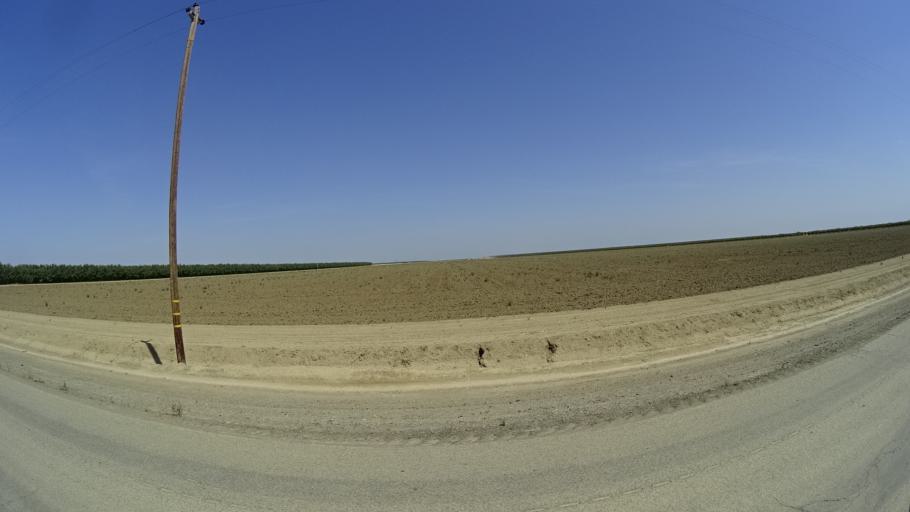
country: US
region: California
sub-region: Fresno County
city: Huron
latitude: 36.1376
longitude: -119.9937
